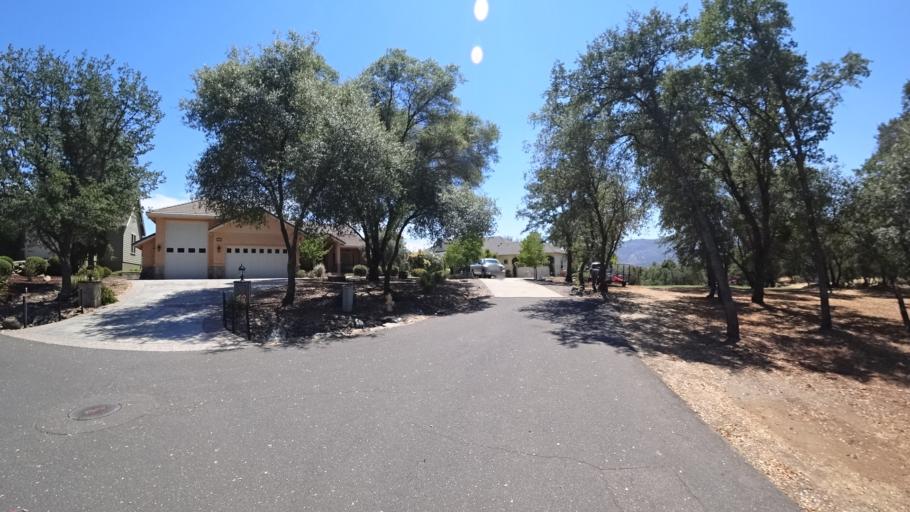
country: US
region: California
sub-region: Calaveras County
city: Angels Camp
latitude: 38.0704
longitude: -120.5616
